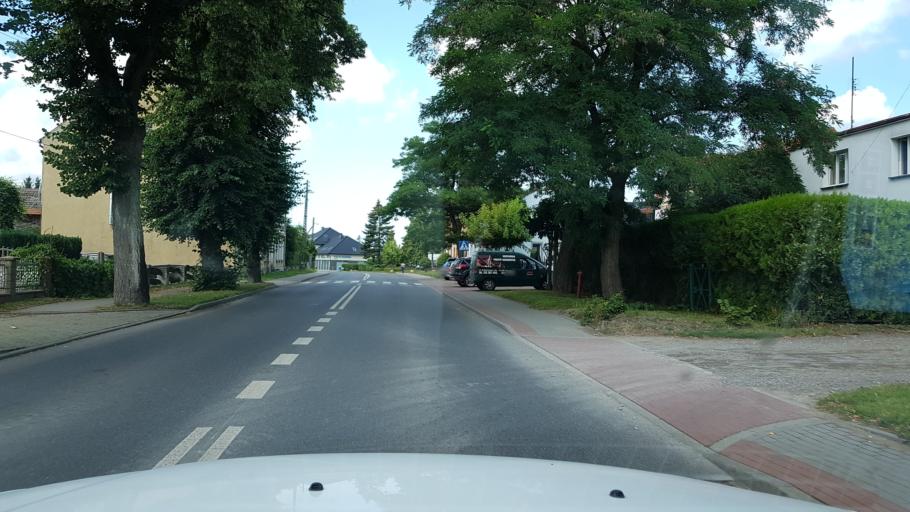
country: PL
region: West Pomeranian Voivodeship
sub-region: Powiat gryficki
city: Trzebiatow
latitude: 54.0649
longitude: 15.2822
